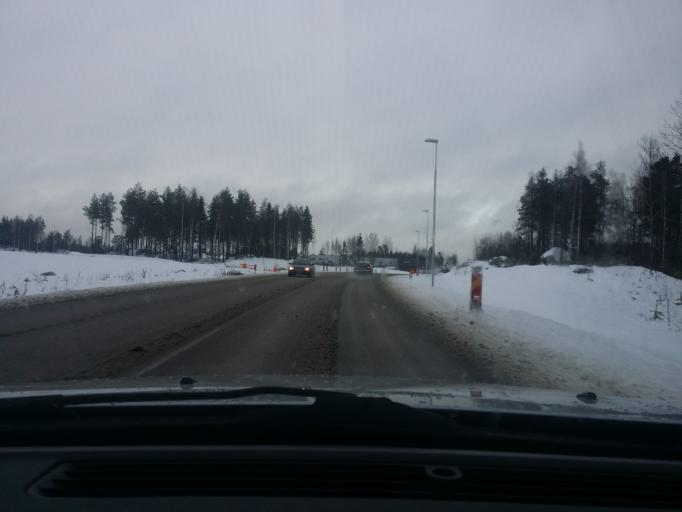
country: SE
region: Vaestmanland
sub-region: Vasteras
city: Vasteras
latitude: 59.5938
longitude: 16.4376
